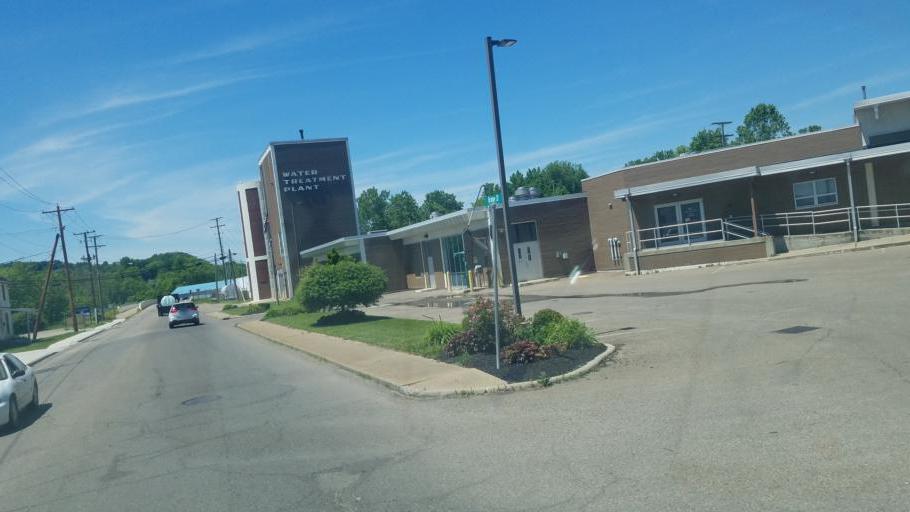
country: US
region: Ohio
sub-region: Coshocton County
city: Coshocton
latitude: 40.2779
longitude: -81.8686
